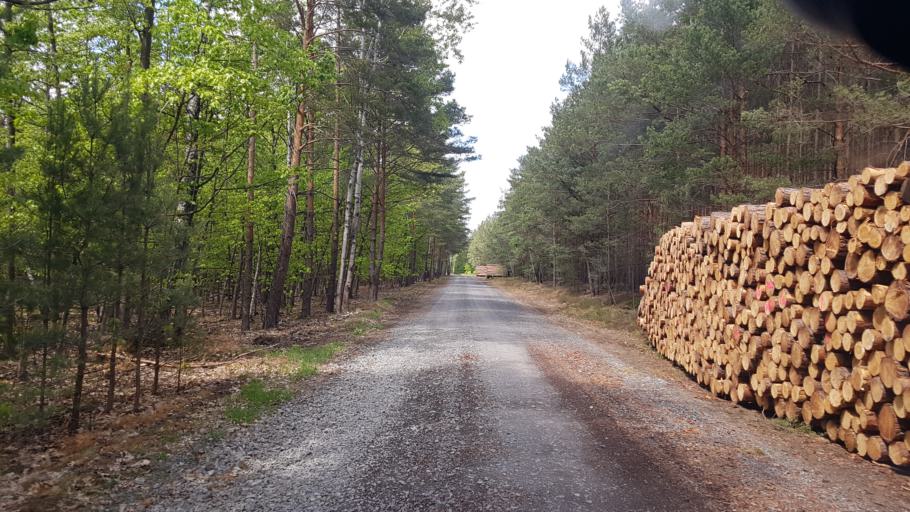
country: DE
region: Brandenburg
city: Altdobern
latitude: 51.6391
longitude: 13.9760
